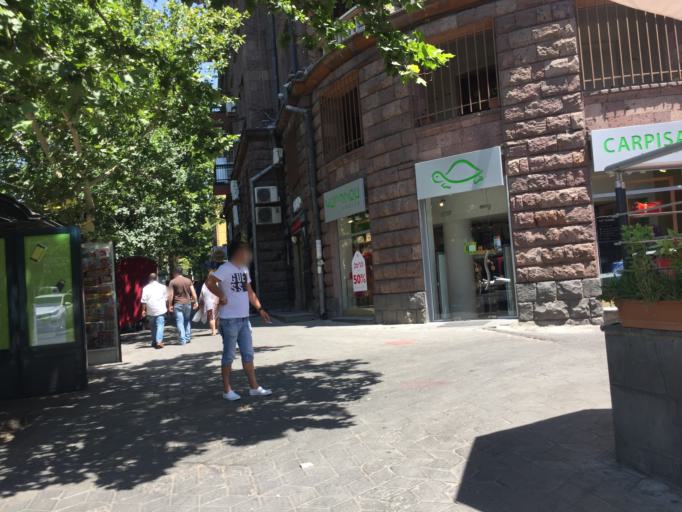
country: AM
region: Yerevan
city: Yerevan
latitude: 40.1848
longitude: 44.5123
